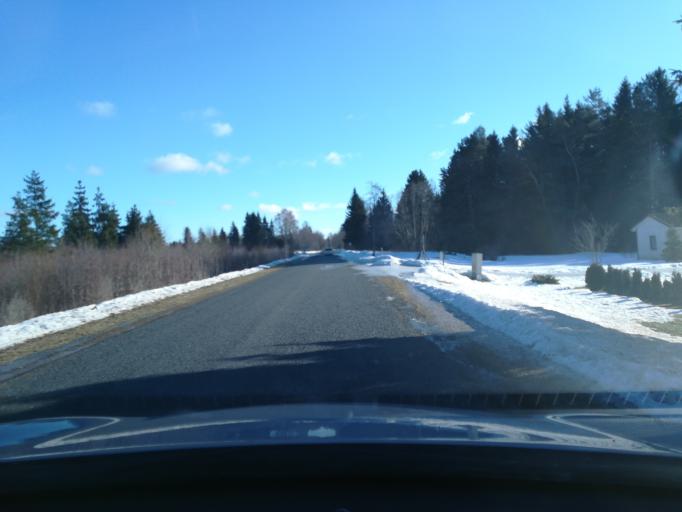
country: EE
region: Raplamaa
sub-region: Kohila vald
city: Kohila
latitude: 59.2341
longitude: 24.7629
